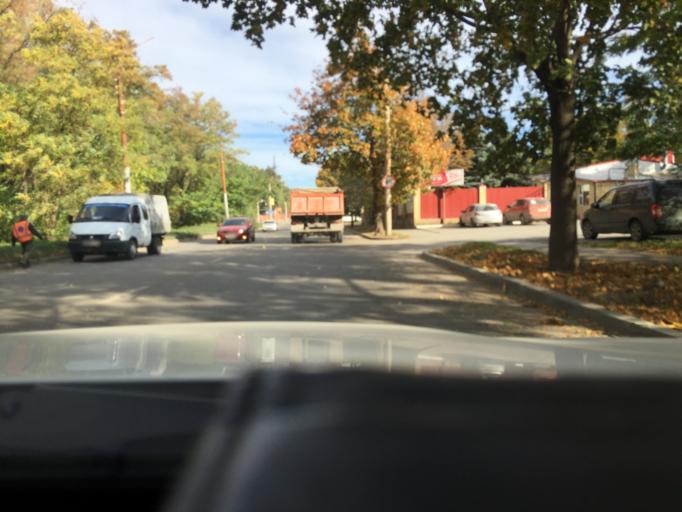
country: RU
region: Rostov
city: Imeni Chkalova
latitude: 47.2874
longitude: 39.8027
